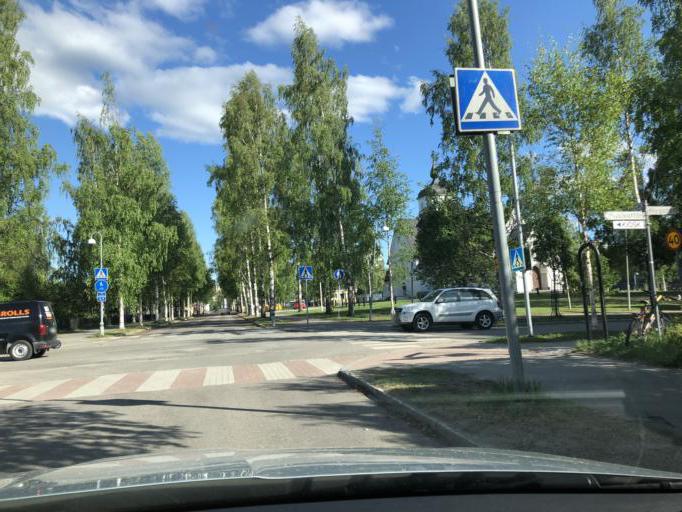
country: SE
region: Norrbotten
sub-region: Pitea Kommun
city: Pitea
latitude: 65.3193
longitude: 21.4828
